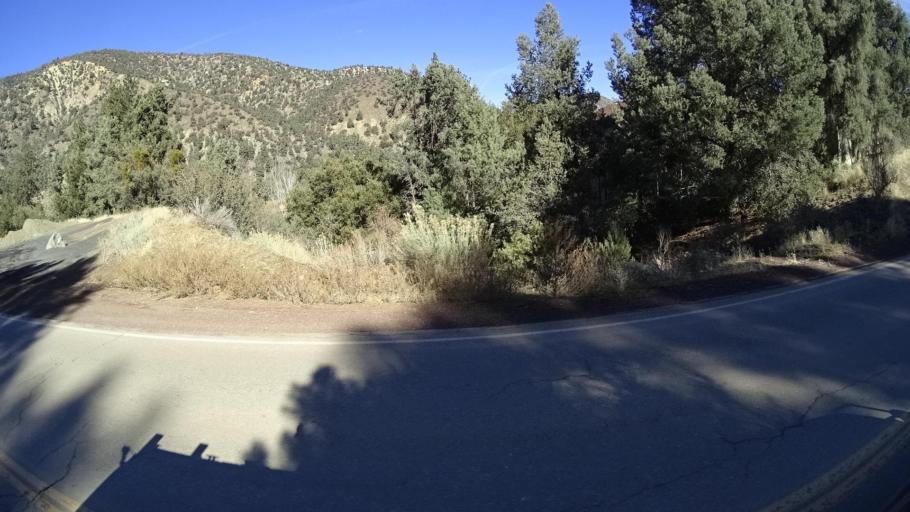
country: US
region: California
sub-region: Kern County
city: Pine Mountain Club
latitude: 34.8525
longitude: -119.1471
